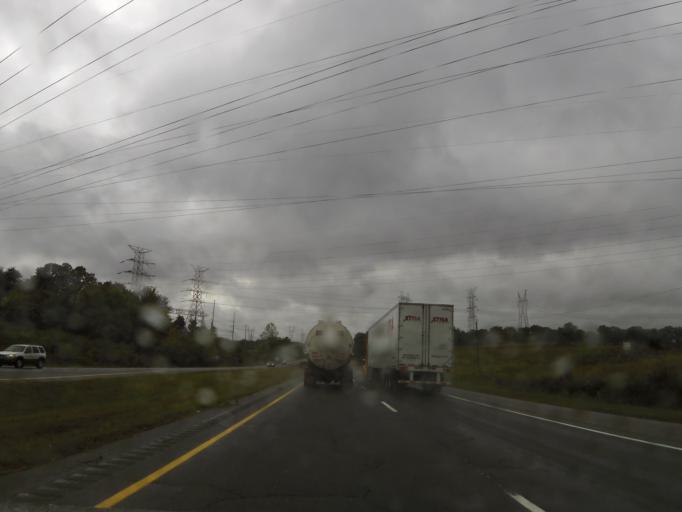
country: US
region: Tennessee
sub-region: Blount County
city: Maryville
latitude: 35.7514
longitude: -84.0007
